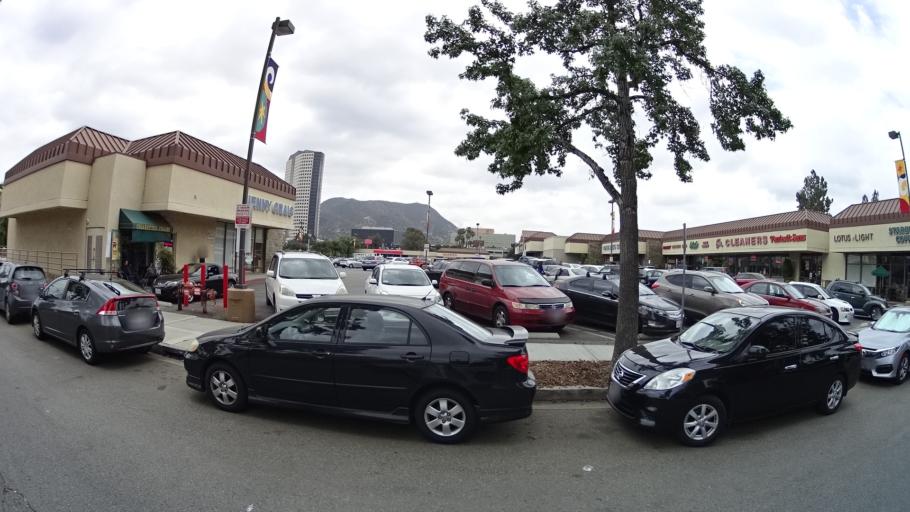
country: US
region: California
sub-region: Los Angeles County
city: Universal City
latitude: 34.1560
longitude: -118.3467
